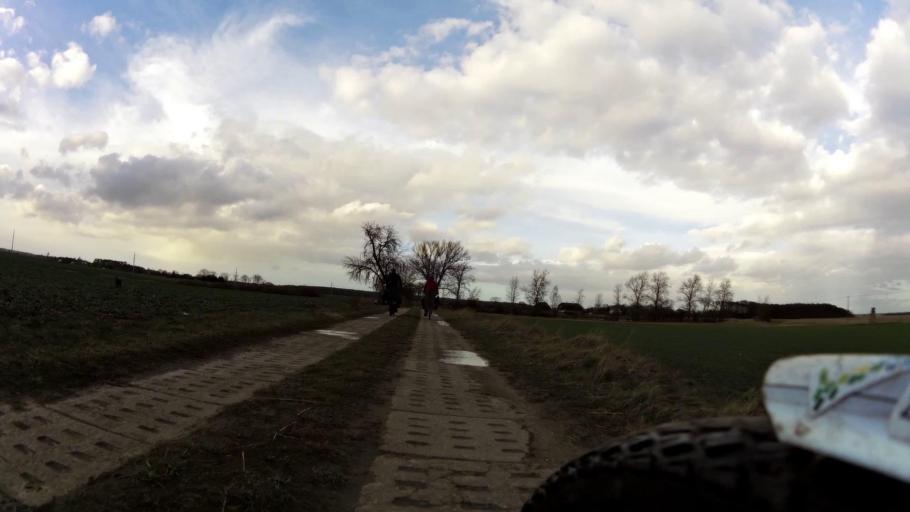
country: PL
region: West Pomeranian Voivodeship
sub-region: Powiat kamienski
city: Kamien Pomorski
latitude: 53.8901
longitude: 14.7196
